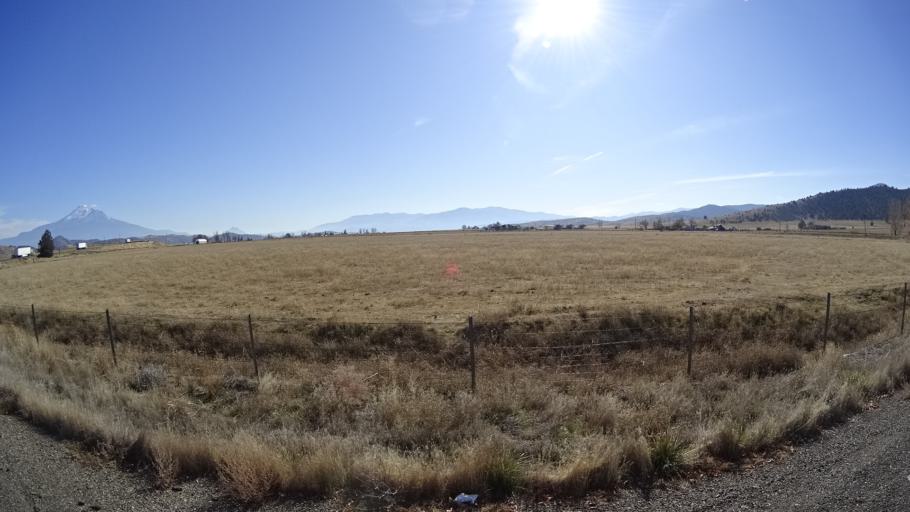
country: US
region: California
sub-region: Siskiyou County
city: Montague
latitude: 41.6326
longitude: -122.5274
